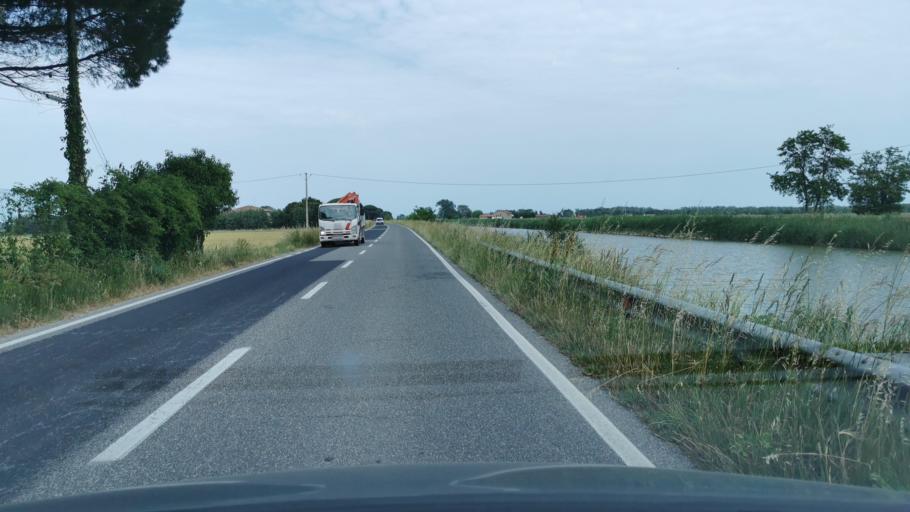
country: IT
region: Emilia-Romagna
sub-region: Provincia di Ravenna
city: Marina Romea
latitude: 44.5584
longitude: 12.2359
